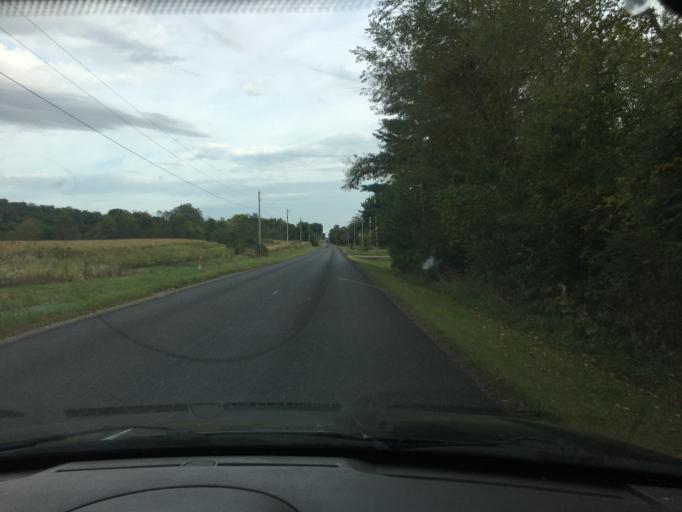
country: US
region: Ohio
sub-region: Logan County
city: Bellefontaine
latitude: 40.3224
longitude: -83.7274
